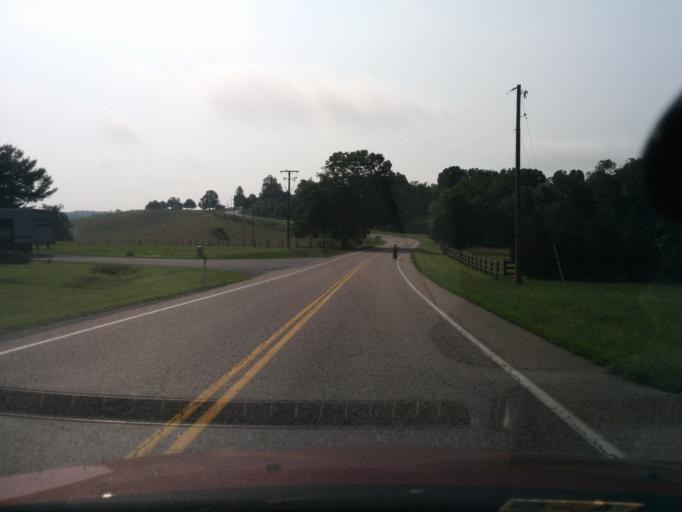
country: US
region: Virginia
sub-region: City of Lexington
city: Lexington
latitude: 37.7581
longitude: -79.4845
